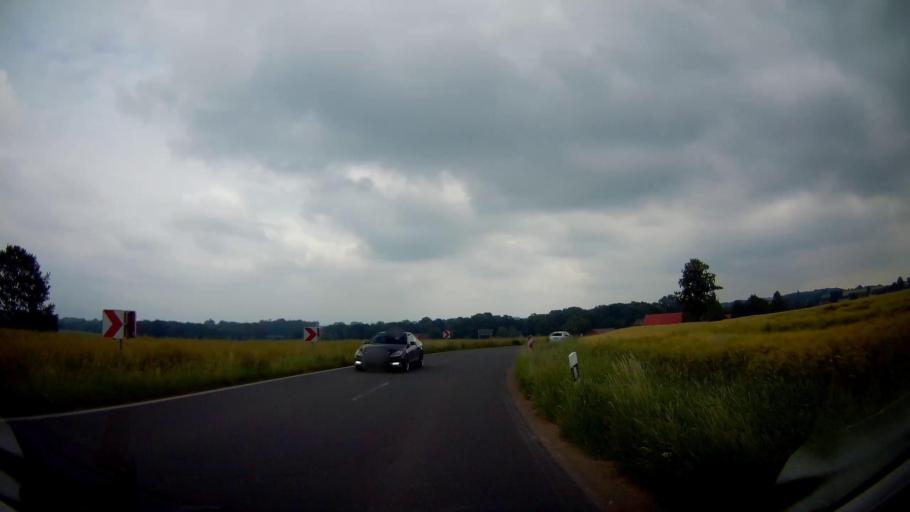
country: DE
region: North Rhine-Westphalia
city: Loehne
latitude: 52.1766
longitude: 8.7387
